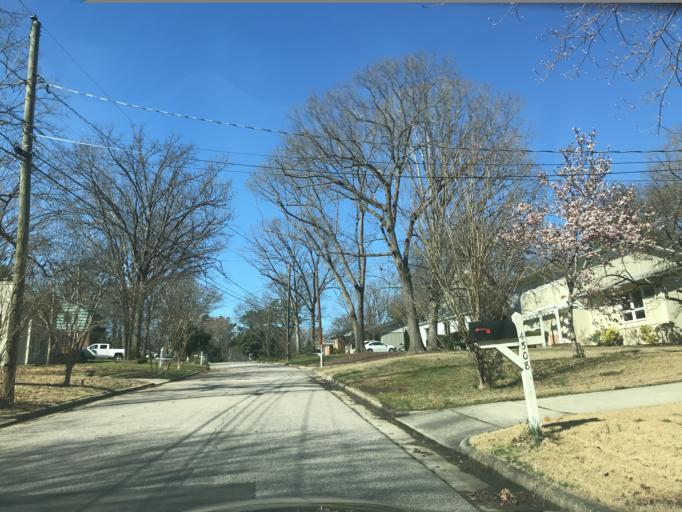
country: US
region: North Carolina
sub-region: Wake County
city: West Raleigh
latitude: 35.8437
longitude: -78.6366
